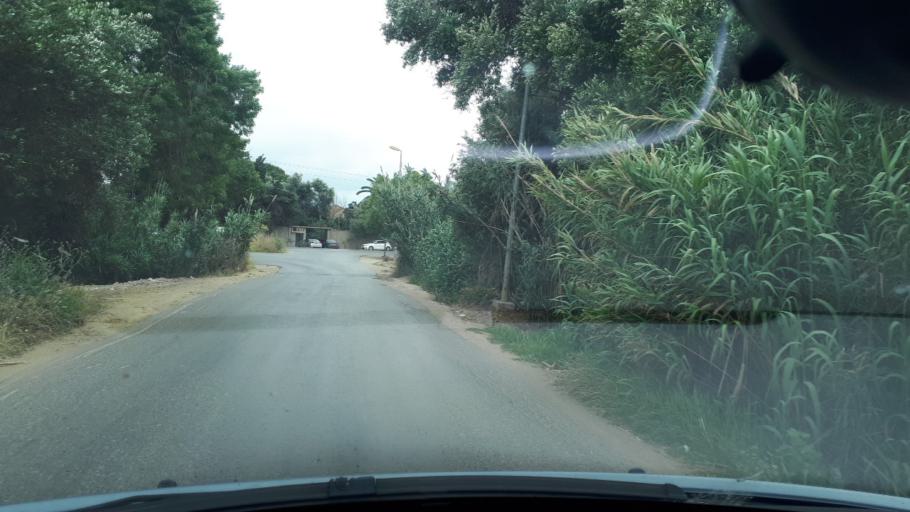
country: DZ
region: Tipaza
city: Cheraga
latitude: 36.7348
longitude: 2.9056
